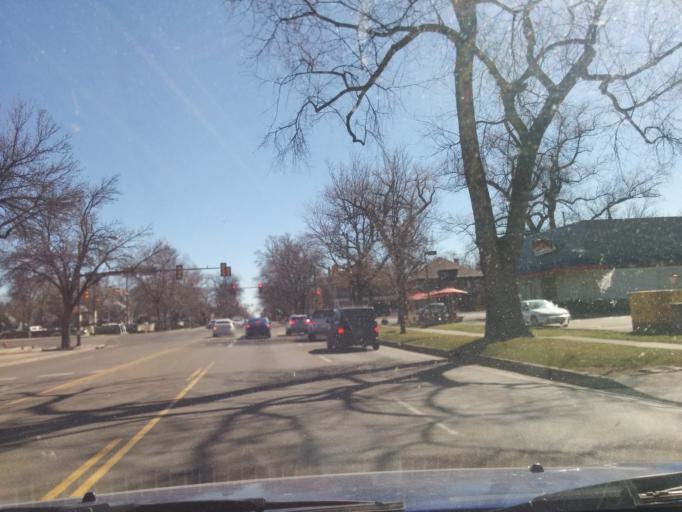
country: US
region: Colorado
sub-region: Larimer County
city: Fort Collins
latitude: 40.5815
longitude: -105.0780
